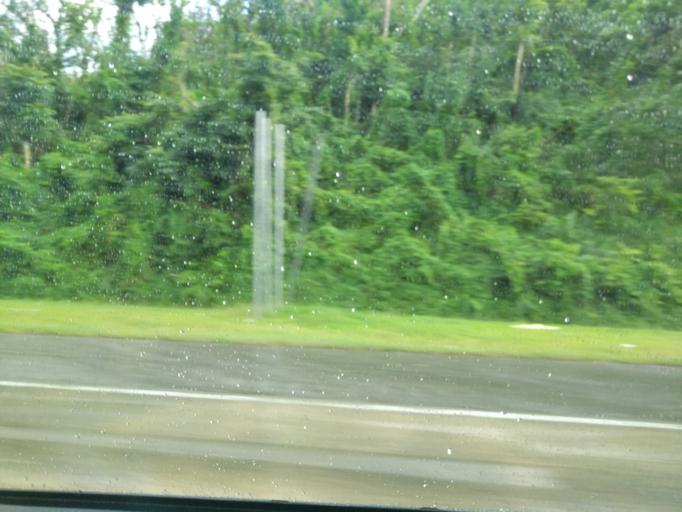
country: PR
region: Cidra
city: Bayamon
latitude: 18.1651
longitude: -66.0834
